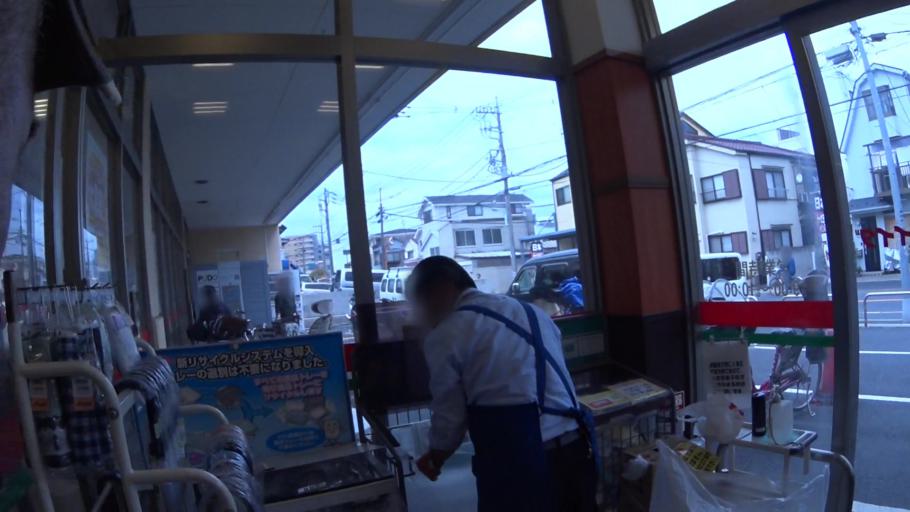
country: JP
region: Tokyo
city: Urayasu
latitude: 35.7123
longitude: 139.8388
